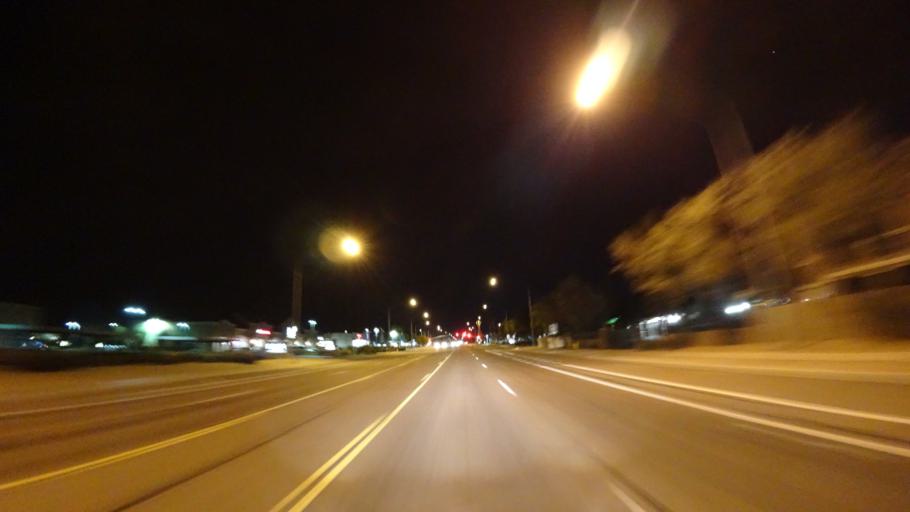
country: US
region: Arizona
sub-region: Maricopa County
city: Gilbert
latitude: 33.3938
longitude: -111.7222
